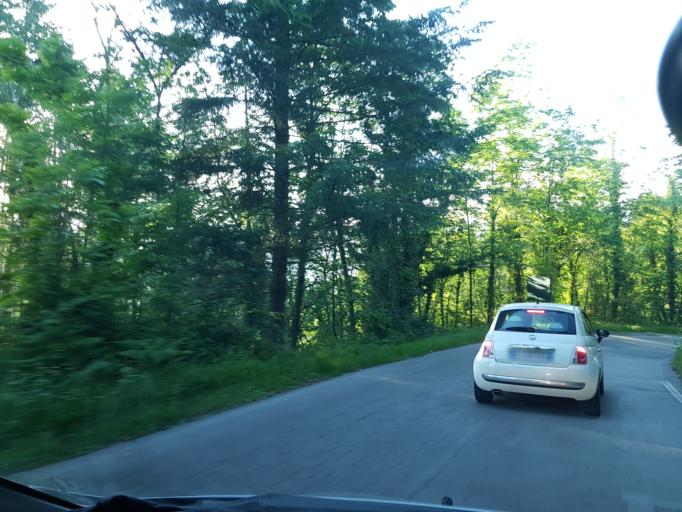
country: IT
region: Tuscany
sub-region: Provincia di Massa-Carrara
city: Casola in Lunigiana
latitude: 44.1898
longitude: 10.1939
